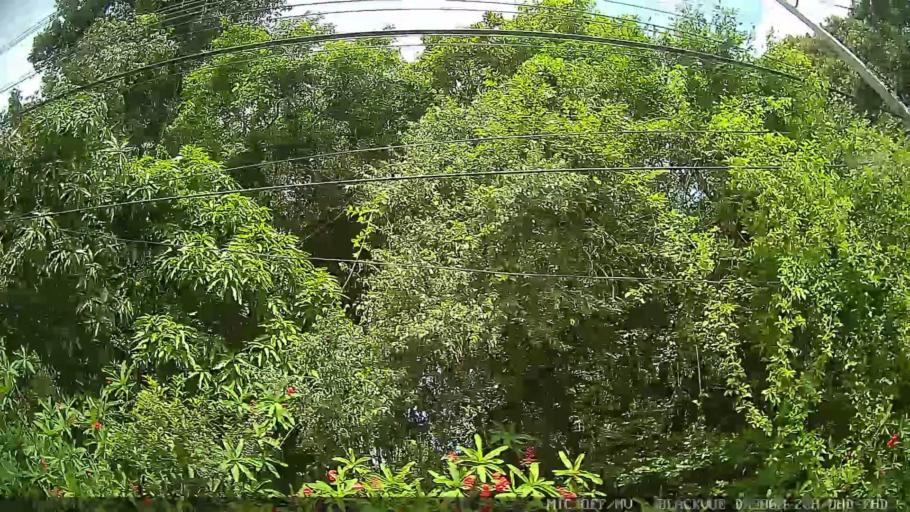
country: BR
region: Sao Paulo
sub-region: Braganca Paulista
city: Braganca Paulista
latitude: -22.9644
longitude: -46.5297
